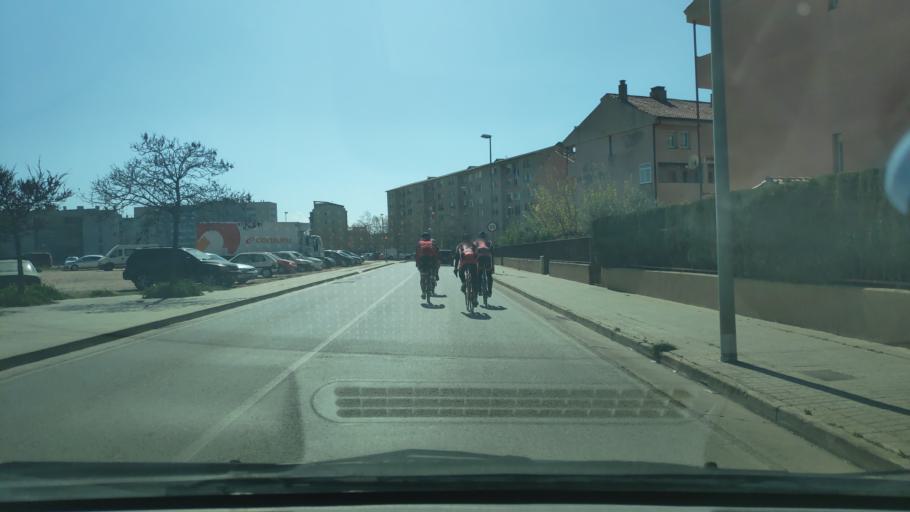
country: ES
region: Catalonia
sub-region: Provincia de Barcelona
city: Sabadell
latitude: 41.5522
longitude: 2.1271
